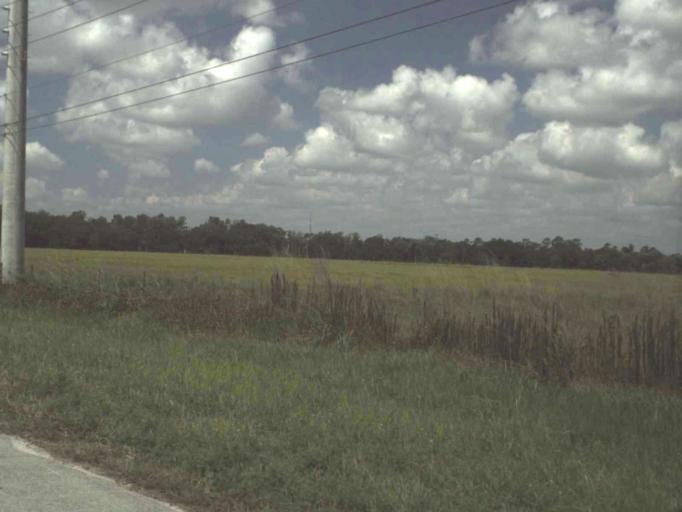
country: US
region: Florida
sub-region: Volusia County
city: Lake Helen
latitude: 28.9037
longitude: -81.1312
